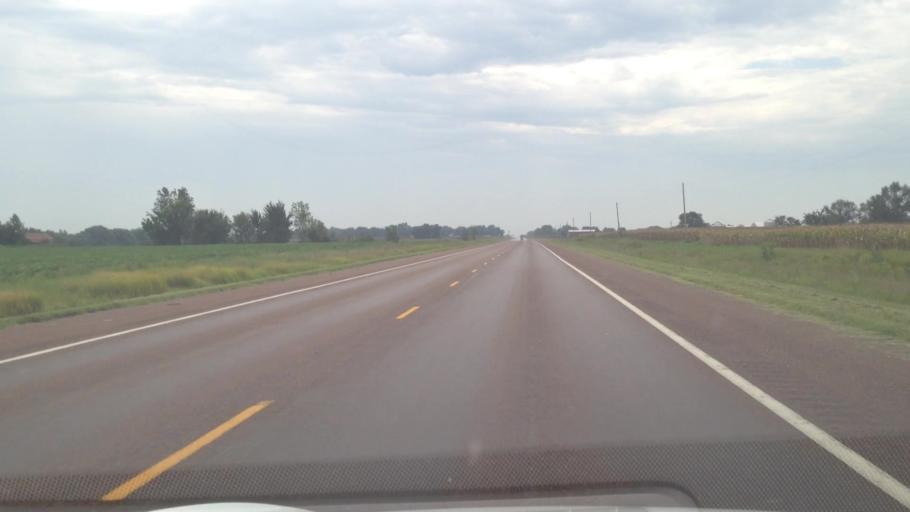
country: US
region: Kansas
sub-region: Crawford County
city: Girard
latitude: 37.4529
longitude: -94.8331
